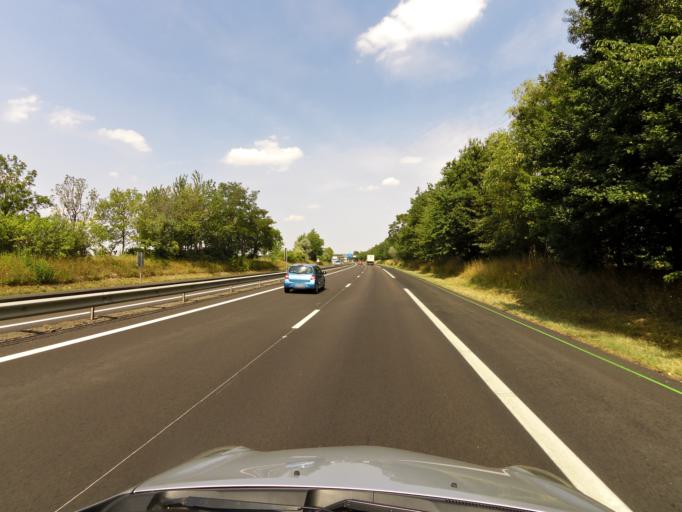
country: FR
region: Champagne-Ardenne
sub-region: Departement de la Marne
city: Saint-Brice-Courcelles
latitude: 49.2943
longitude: 3.9925
